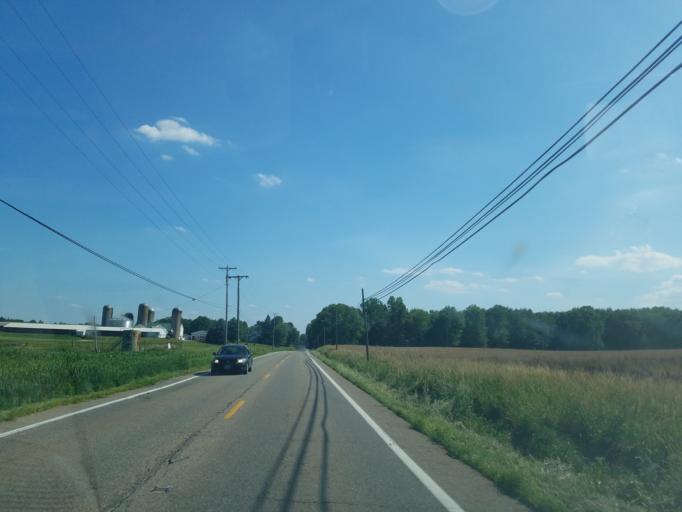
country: US
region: Ohio
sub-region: Portage County
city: Ravenna
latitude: 41.1965
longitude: -81.2462
